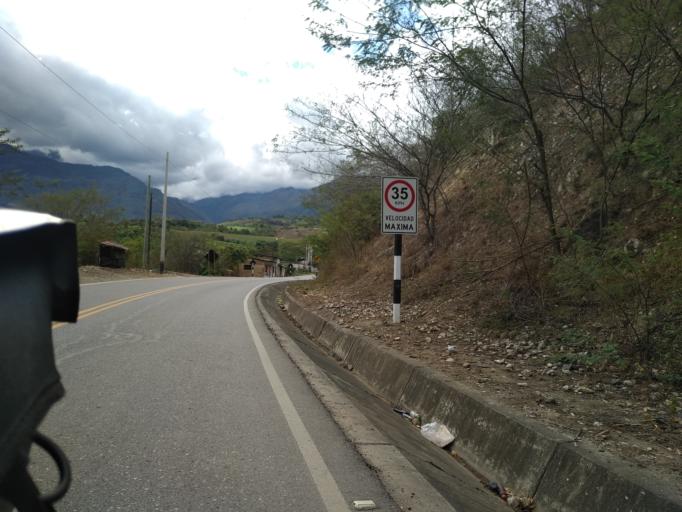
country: PE
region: Amazonas
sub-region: Utcubamba
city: Jamalca
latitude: -5.8371
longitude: -78.2426
